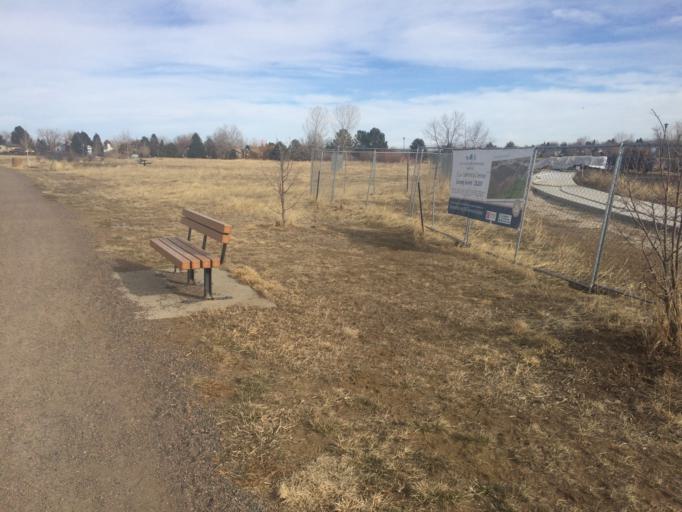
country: US
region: Colorado
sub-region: Broomfield County
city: Broomfield
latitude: 39.9218
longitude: -105.0657
